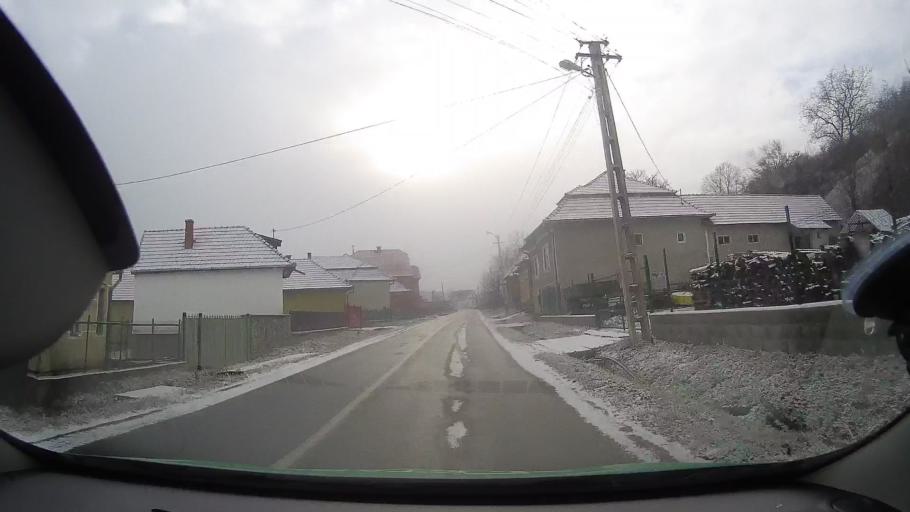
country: RO
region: Alba
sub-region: Comuna Rimetea
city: Rimetea
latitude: 46.4260
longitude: 23.5618
